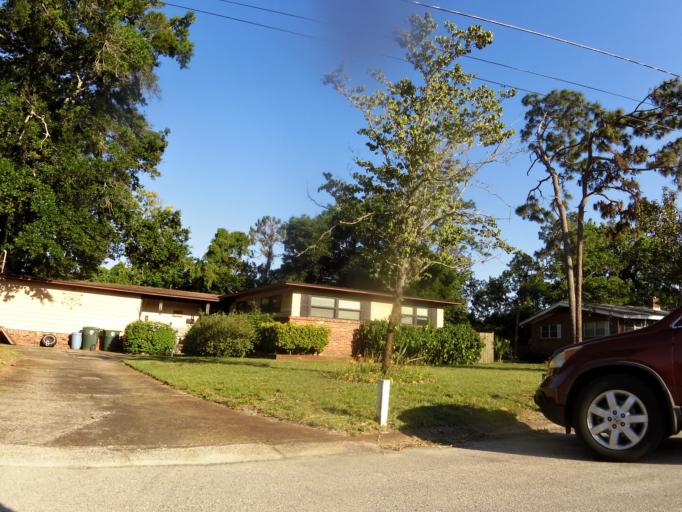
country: US
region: Florida
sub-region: Duval County
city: Jacksonville
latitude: 30.2400
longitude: -81.6138
